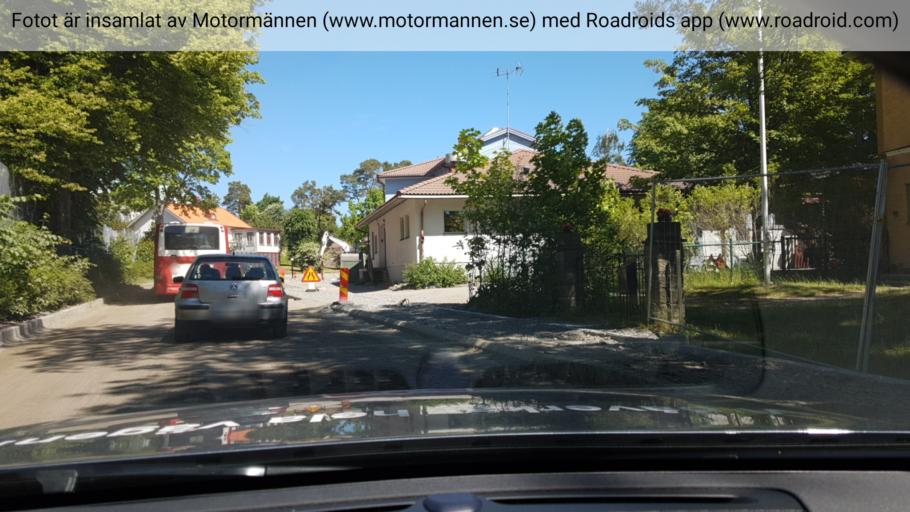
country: SE
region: Stockholm
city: Dalaro
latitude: 59.1342
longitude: 18.4092
